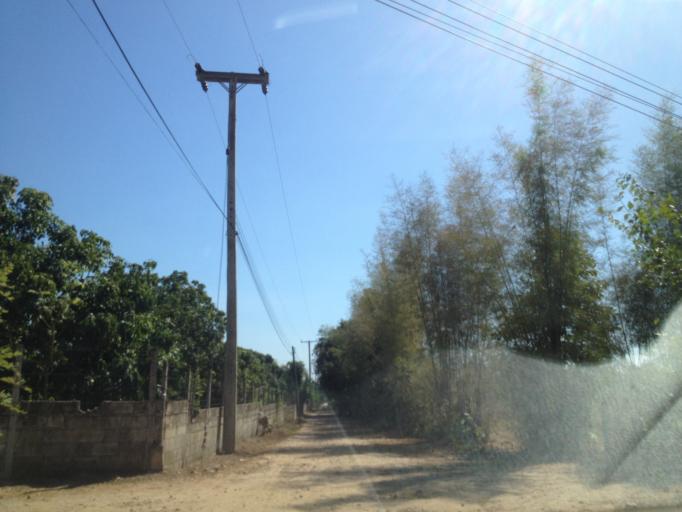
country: TH
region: Chiang Mai
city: San Pa Tong
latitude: 18.6678
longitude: 98.8728
